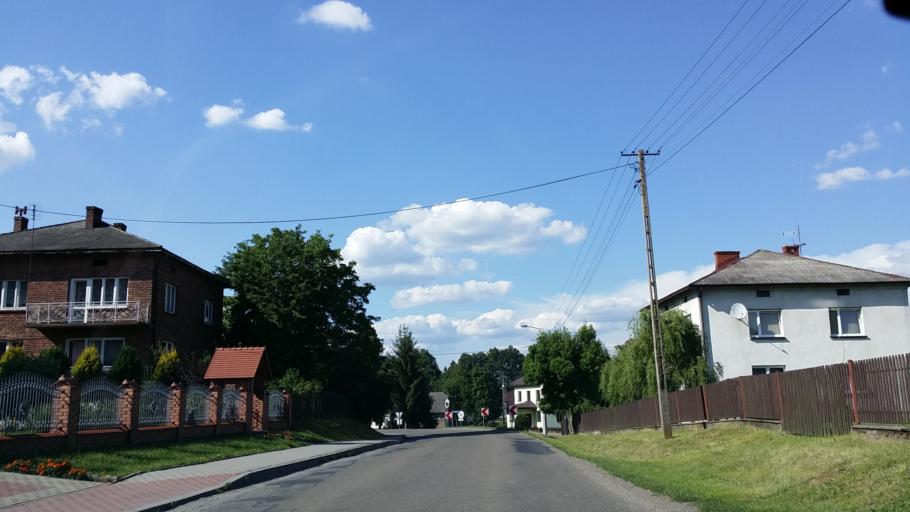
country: PL
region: Lesser Poland Voivodeship
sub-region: Powiat wadowicki
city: Spytkowice
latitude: 49.9837
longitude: 19.5018
